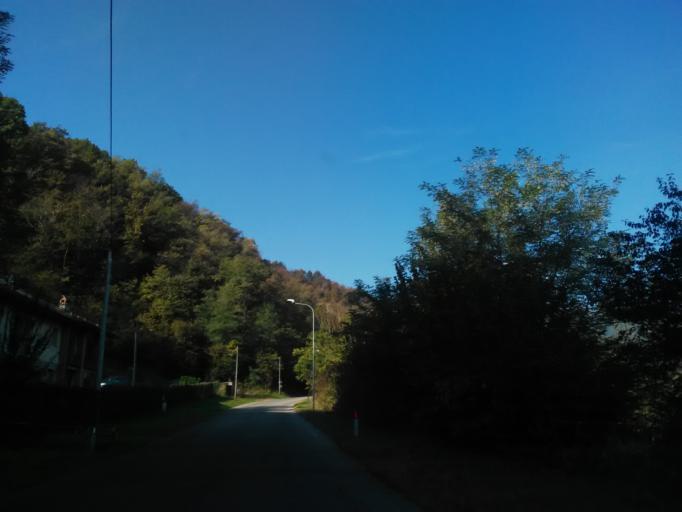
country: IT
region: Piedmont
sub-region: Provincia di Vercelli
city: Guardabosone
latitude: 45.6958
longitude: 8.2461
